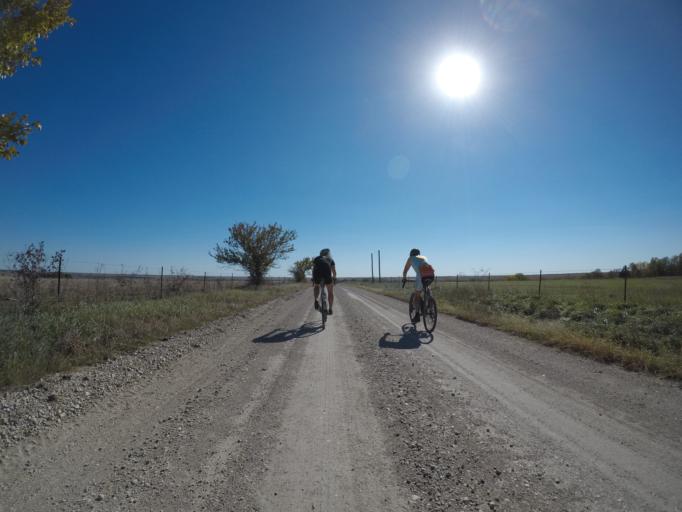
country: US
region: Kansas
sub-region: Wabaunsee County
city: Alma
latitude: 38.9662
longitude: -96.4735
